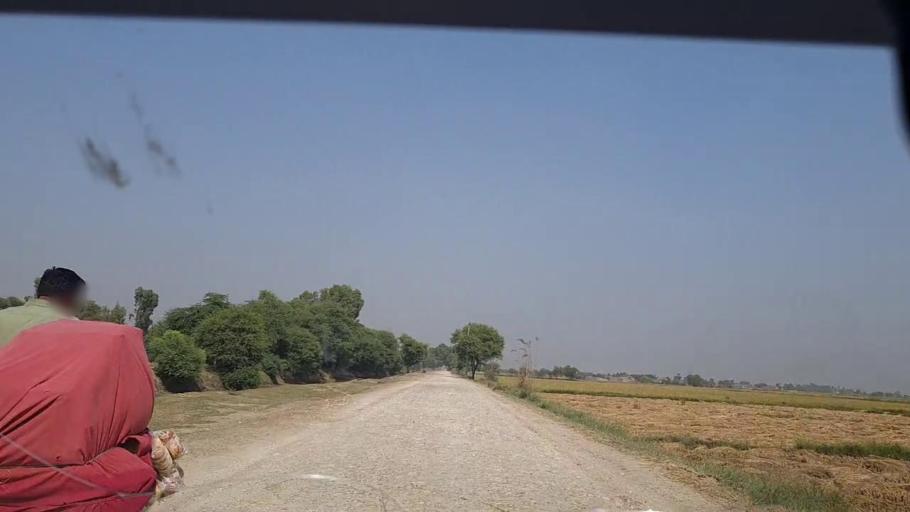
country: PK
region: Sindh
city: Thul
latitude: 28.1065
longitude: 68.6916
